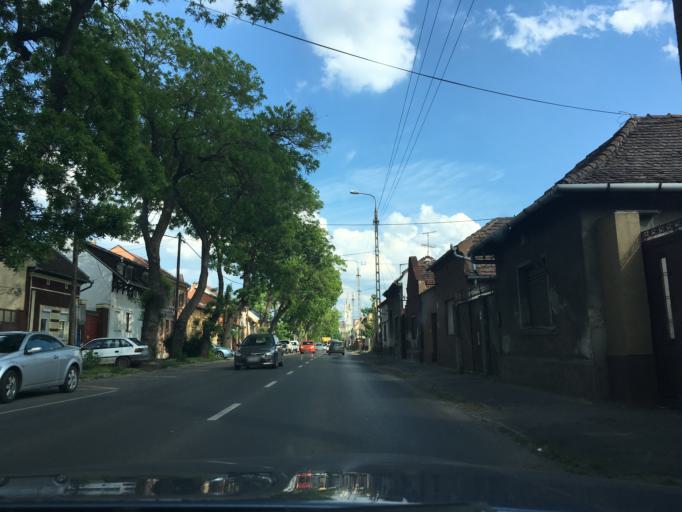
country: HU
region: Hajdu-Bihar
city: Debrecen
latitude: 47.5401
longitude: 21.6317
